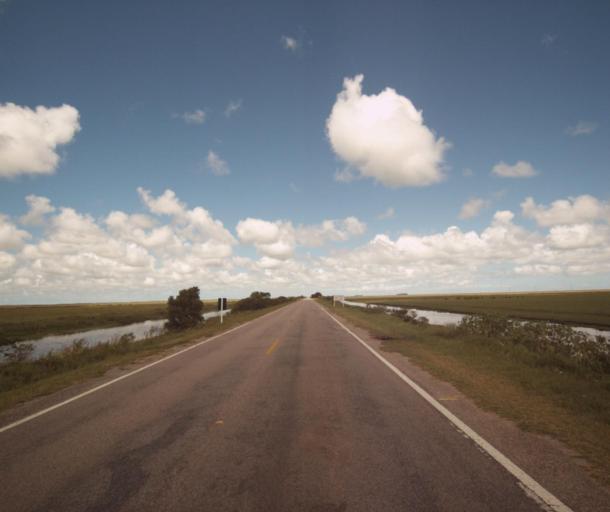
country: BR
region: Rio Grande do Sul
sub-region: Arroio Grande
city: Arroio Grande
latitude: -32.5548
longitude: -52.5492
